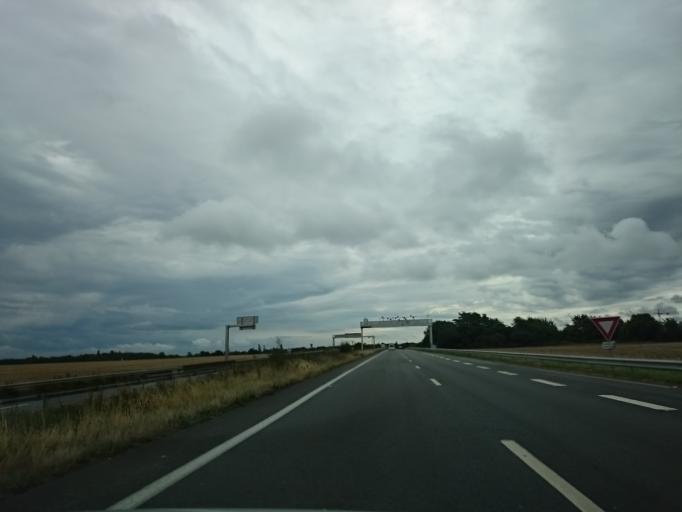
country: FR
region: Ile-de-France
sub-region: Departement de l'Essonne
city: Saclay
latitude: 48.7217
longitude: 2.1683
